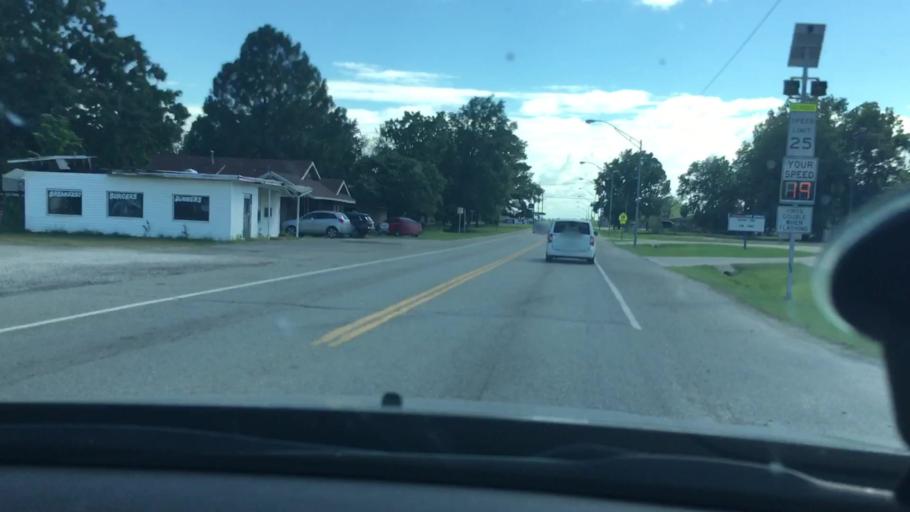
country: US
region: Oklahoma
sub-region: Sequoyah County
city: Vian
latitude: 35.4970
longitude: -94.9701
